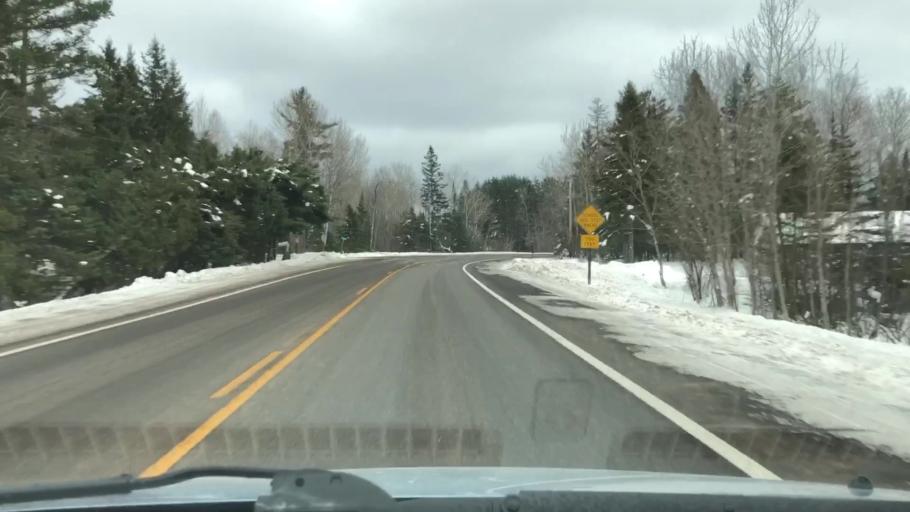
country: US
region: Minnesota
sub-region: Carlton County
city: Esko
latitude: 46.6857
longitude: -92.3648
